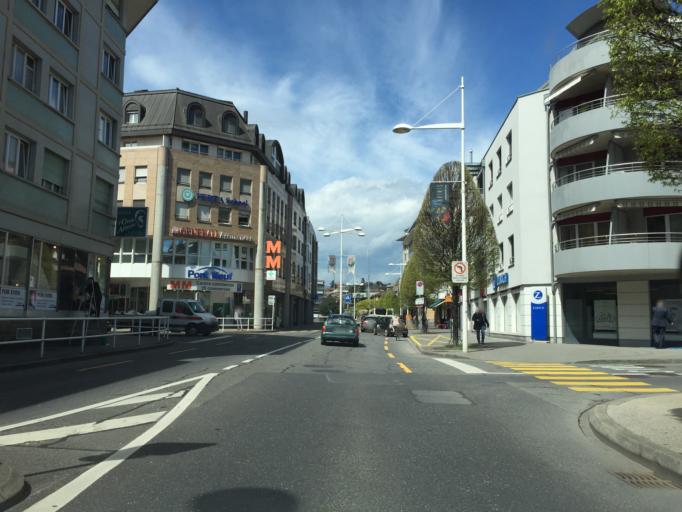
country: CH
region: Vaud
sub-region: Morges District
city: Morges
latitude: 46.5095
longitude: 6.4955
